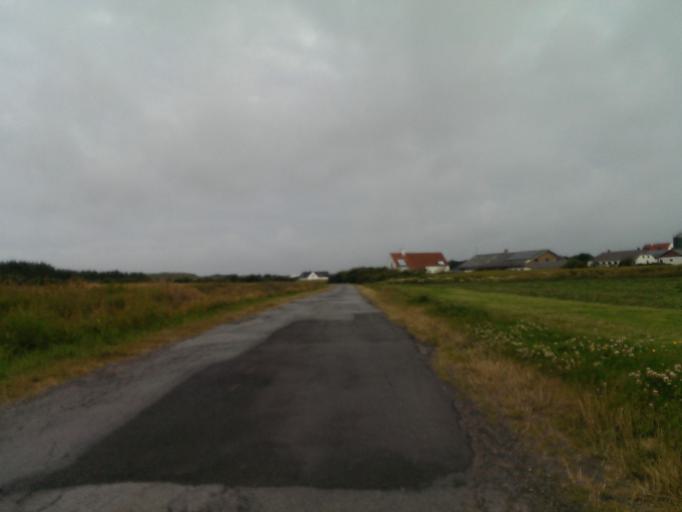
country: DK
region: North Denmark
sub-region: Jammerbugt Kommune
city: Pandrup
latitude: 57.3794
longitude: 9.7342
